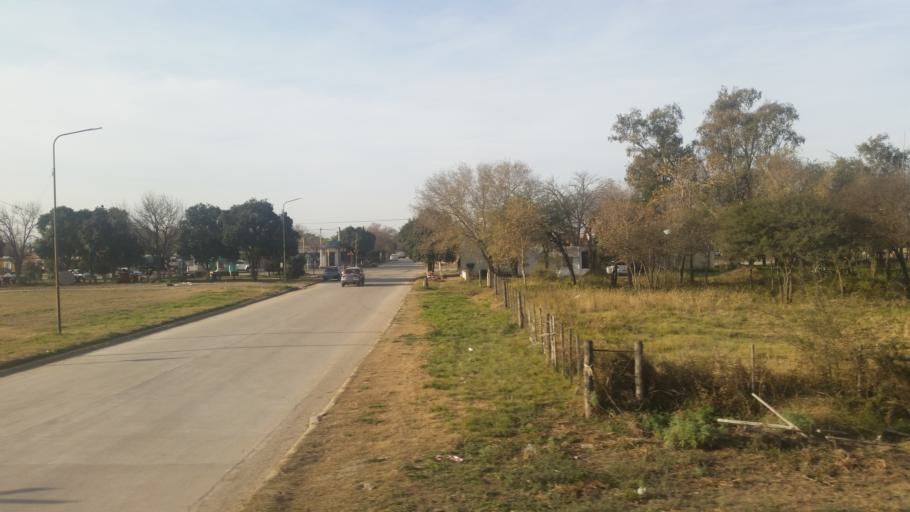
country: AR
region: Cordoba
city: Toledo
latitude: -31.5581
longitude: -64.0075
